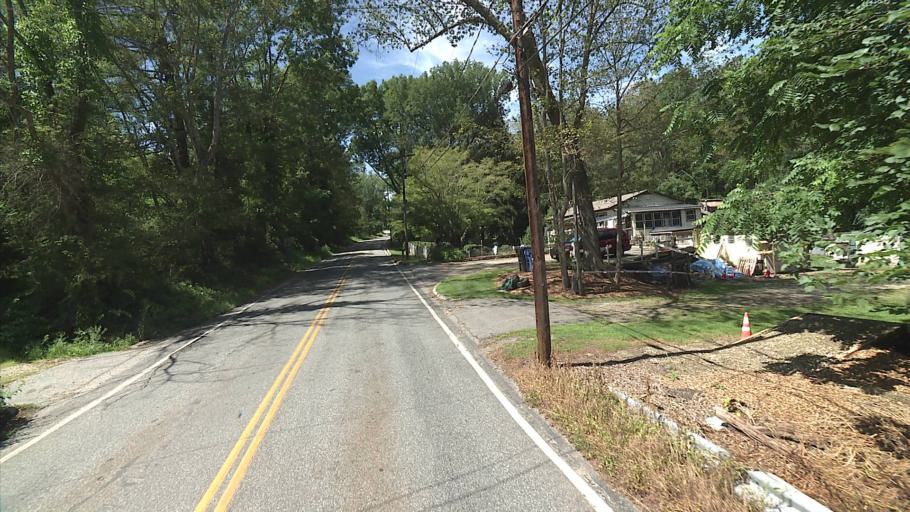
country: US
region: Connecticut
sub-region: Windham County
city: South Woodstock
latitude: 41.8734
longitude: -71.9674
